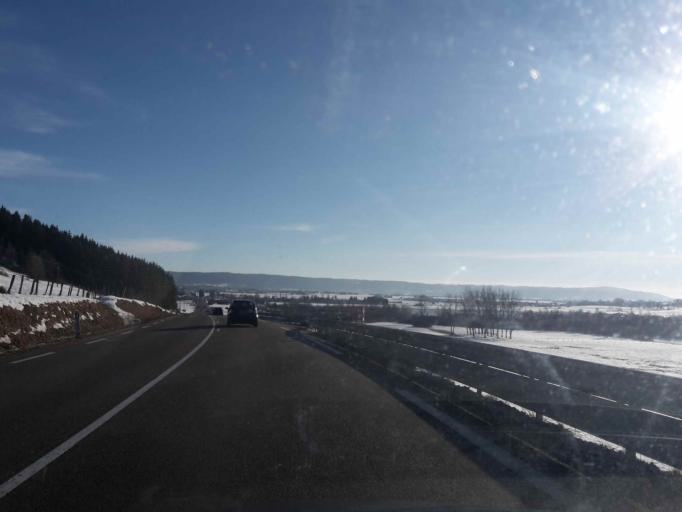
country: FR
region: Franche-Comte
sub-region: Departement du Doubs
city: Doubs
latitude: 46.9576
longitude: 6.3415
